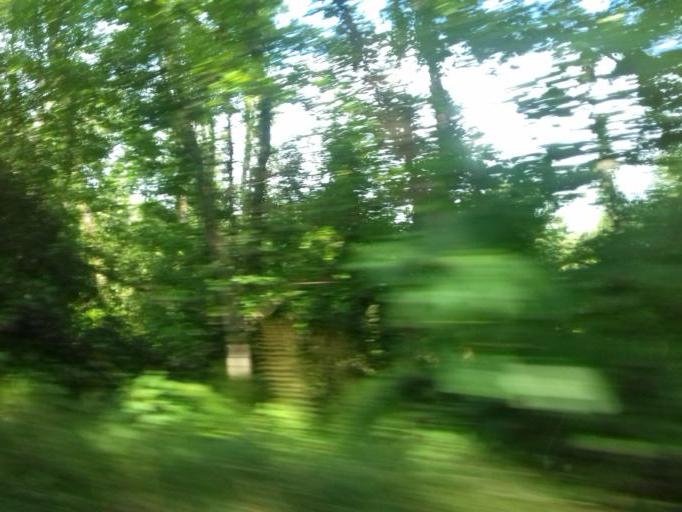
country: IE
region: Leinster
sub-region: Loch Garman
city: Loch Garman
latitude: 52.2925
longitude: -6.6416
